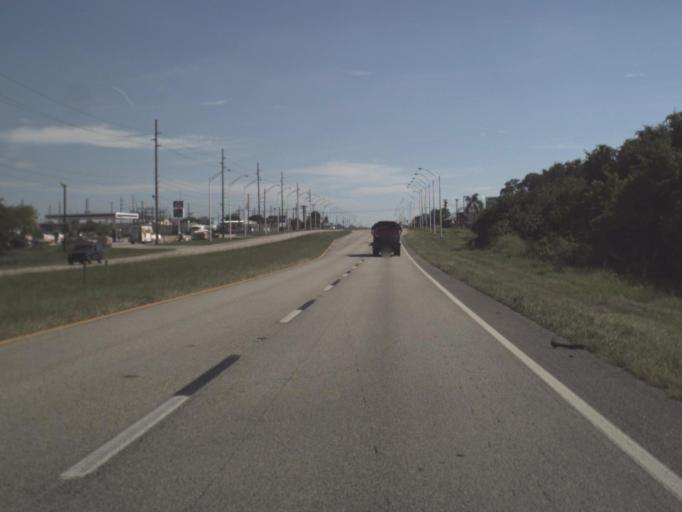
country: US
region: Florida
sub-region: Highlands County
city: Lake Placid
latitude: 27.2712
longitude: -81.3502
